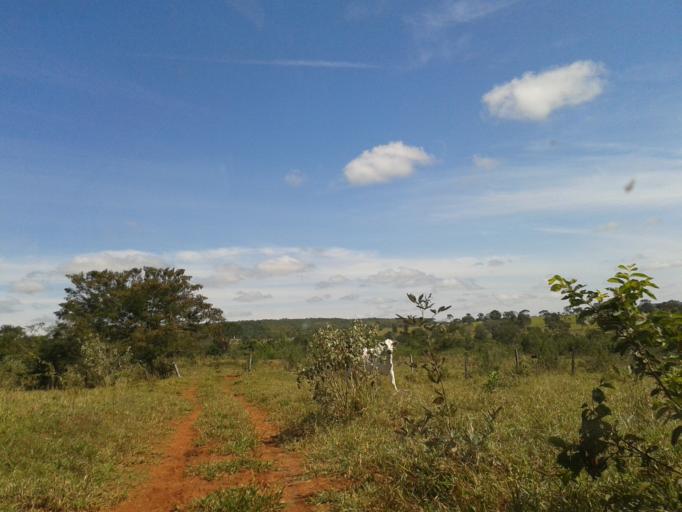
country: BR
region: Minas Gerais
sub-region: Campina Verde
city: Campina Verde
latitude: -19.4340
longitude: -49.7018
